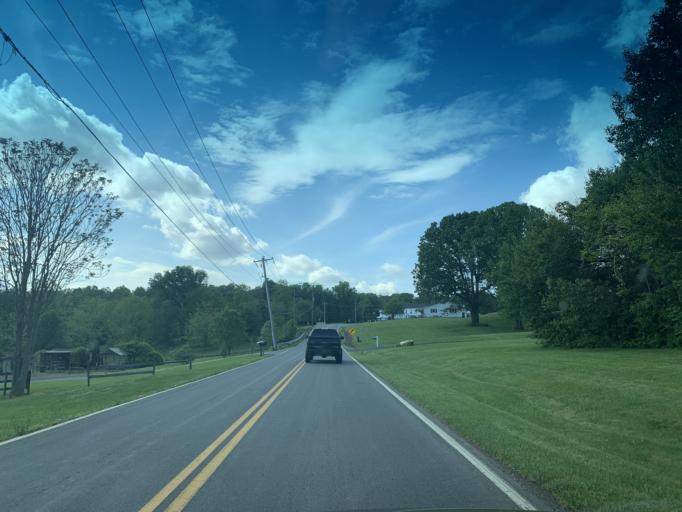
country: US
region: Maryland
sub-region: Cecil County
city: Rising Sun
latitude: 39.6992
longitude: -76.1430
